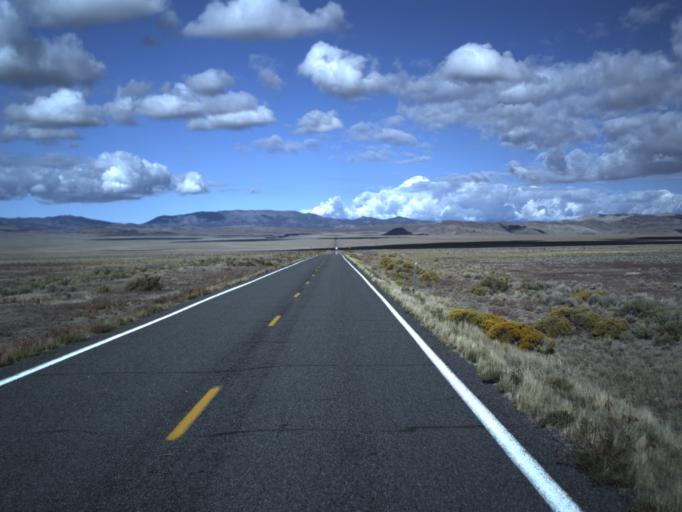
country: US
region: Utah
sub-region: Beaver County
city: Milford
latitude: 38.5384
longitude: -113.6983
